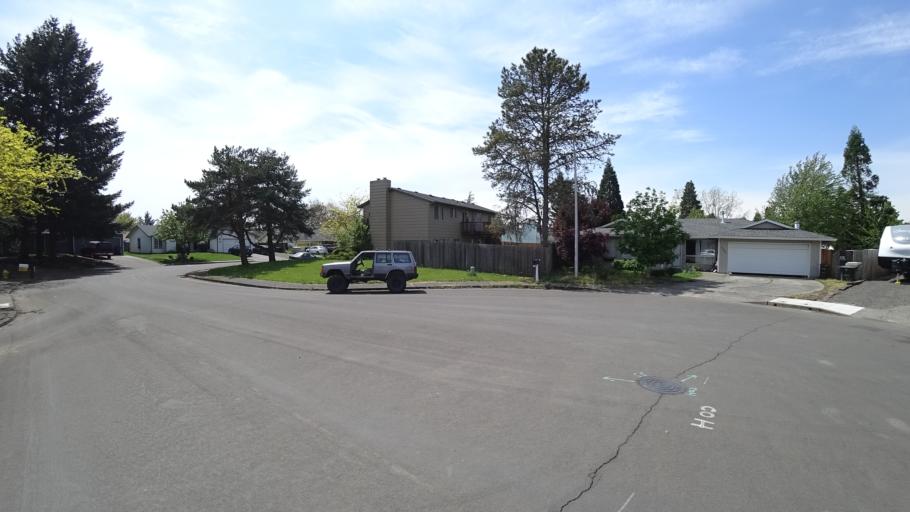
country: US
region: Oregon
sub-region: Washington County
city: Aloha
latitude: 45.5021
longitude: -122.9256
